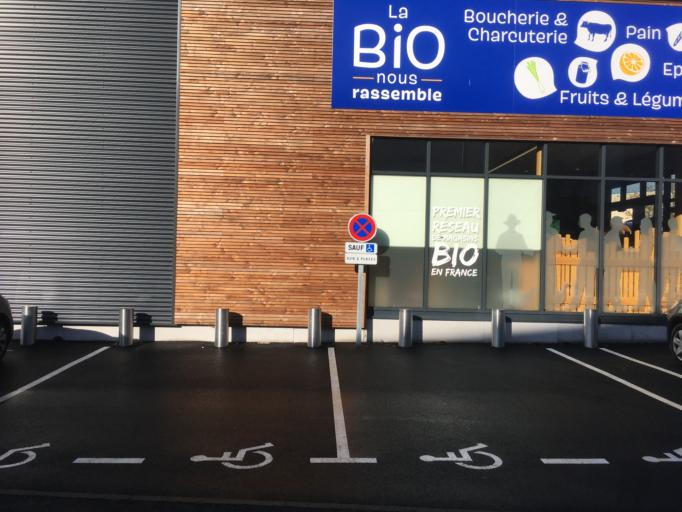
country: FR
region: Pays de la Loire
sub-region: Departement de la Loire-Atlantique
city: Clisson
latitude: 47.0985
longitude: -1.2811
